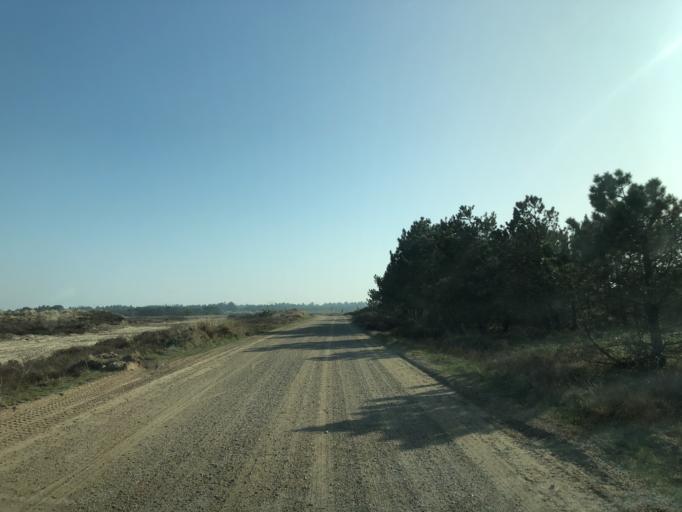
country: DK
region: South Denmark
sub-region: Varde Kommune
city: Oksbol
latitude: 55.5686
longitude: 8.1367
